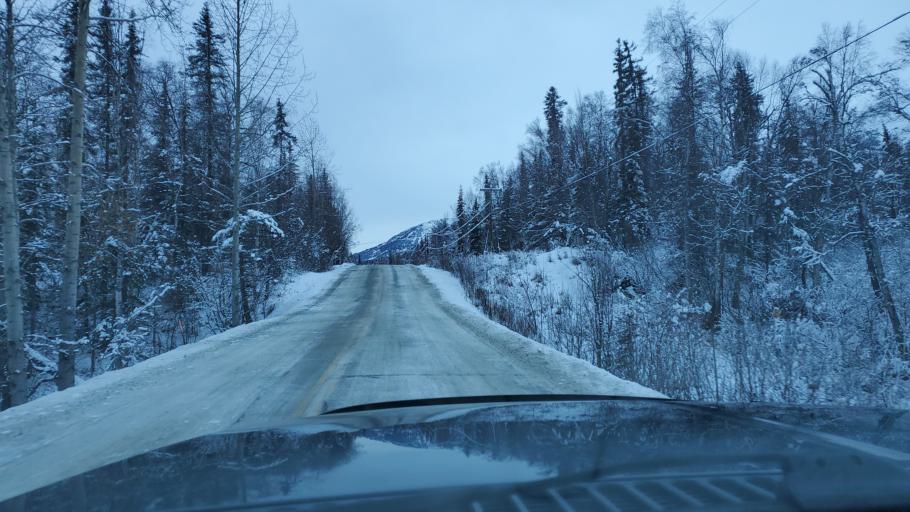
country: US
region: Alaska
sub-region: Matanuska-Susitna Borough
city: Lakes
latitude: 61.6933
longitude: -149.3153
